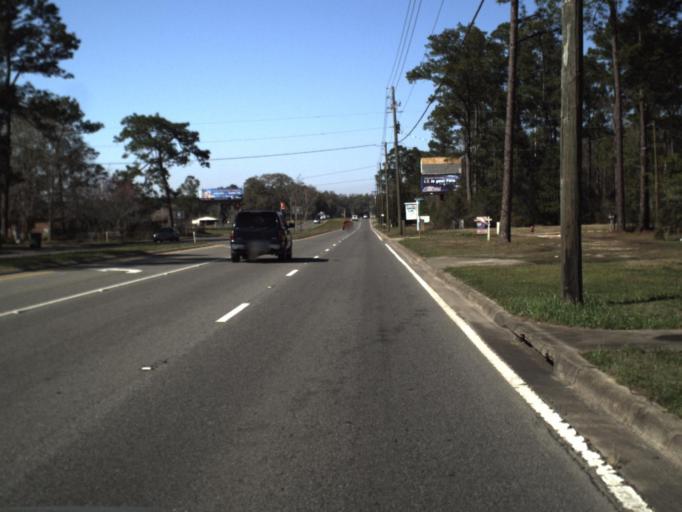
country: US
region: Florida
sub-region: Jackson County
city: Marianna
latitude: 30.7422
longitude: -85.1860
